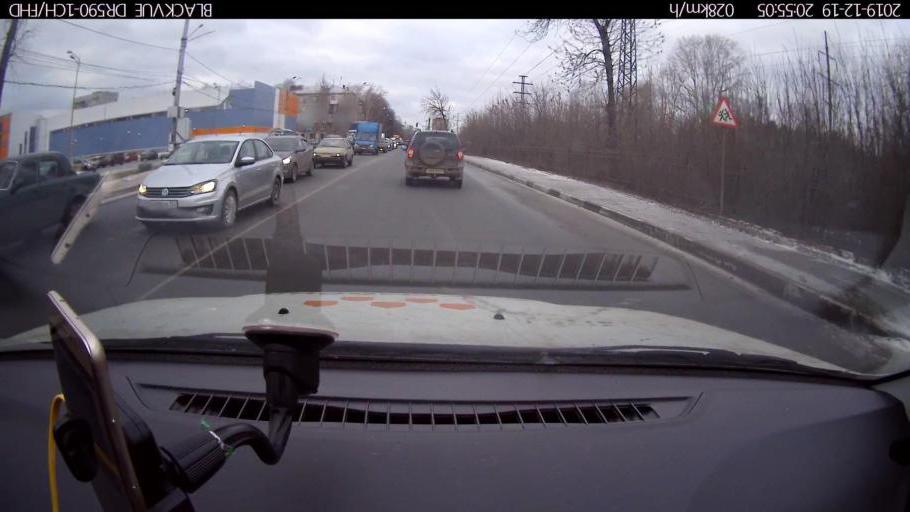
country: RU
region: Nizjnij Novgorod
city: Gorbatovka
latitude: 56.3321
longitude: 43.8613
